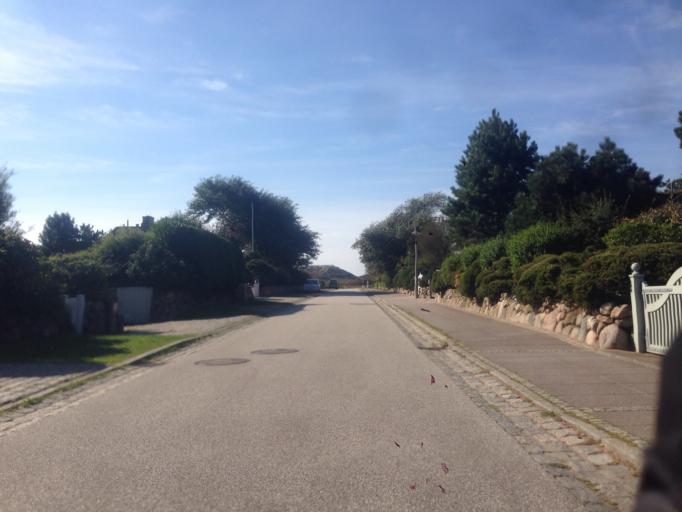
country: DE
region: Schleswig-Holstein
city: Tinnum
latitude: 54.9542
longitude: 8.3400
